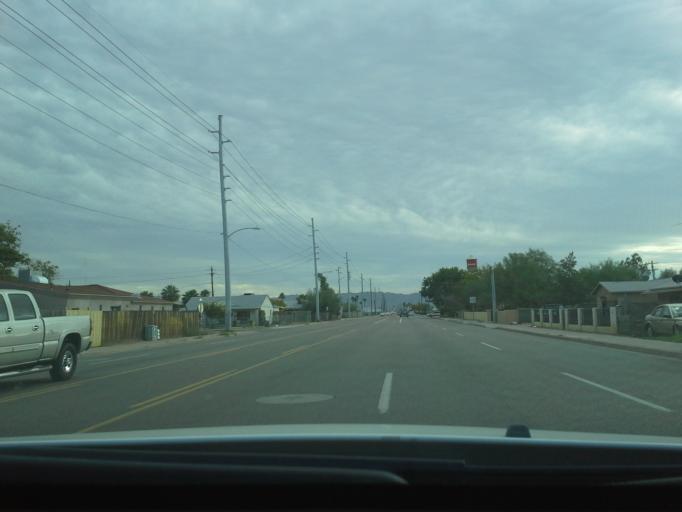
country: US
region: Arizona
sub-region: Maricopa County
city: Phoenix
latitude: 33.4489
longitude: -112.1176
